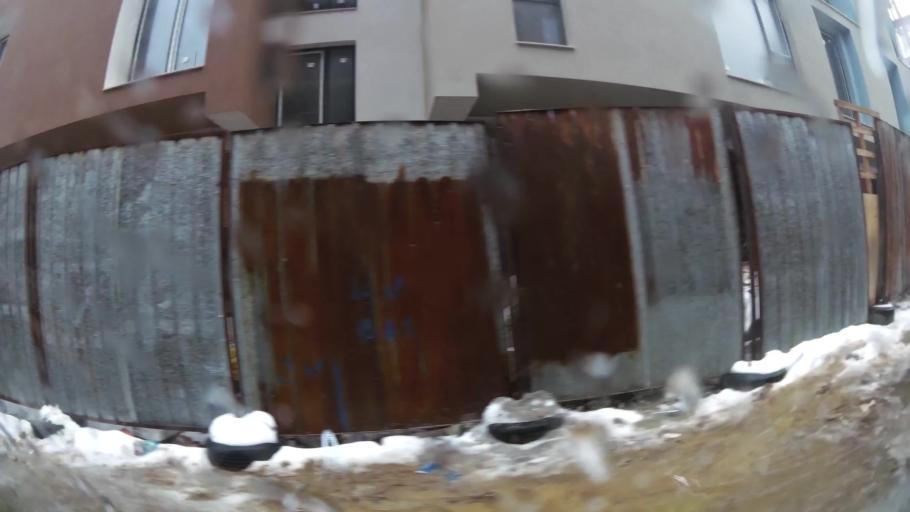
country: BG
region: Sofia-Capital
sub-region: Stolichna Obshtina
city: Sofia
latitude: 42.6799
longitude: 23.2589
